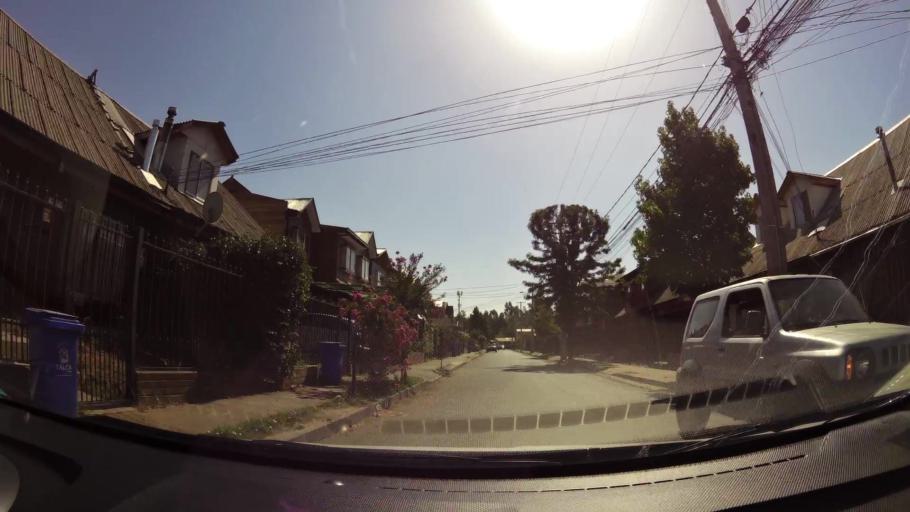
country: CL
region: Maule
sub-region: Provincia de Talca
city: Talca
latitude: -35.4096
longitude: -71.6375
